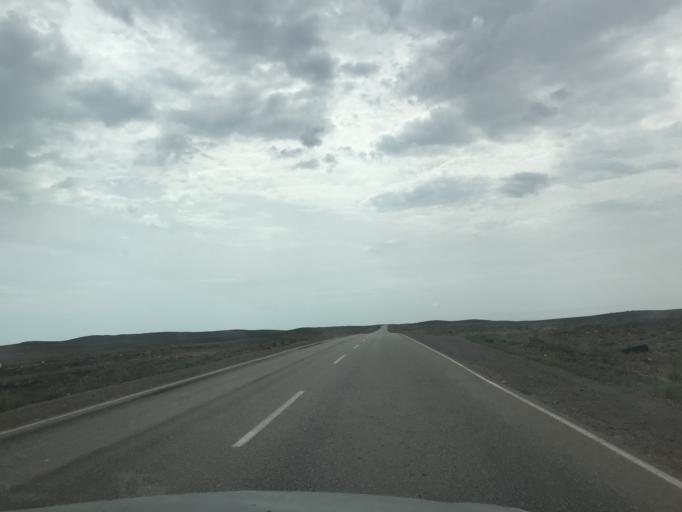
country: KZ
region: Zhambyl
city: Mynaral
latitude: 45.4897
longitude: 73.5309
